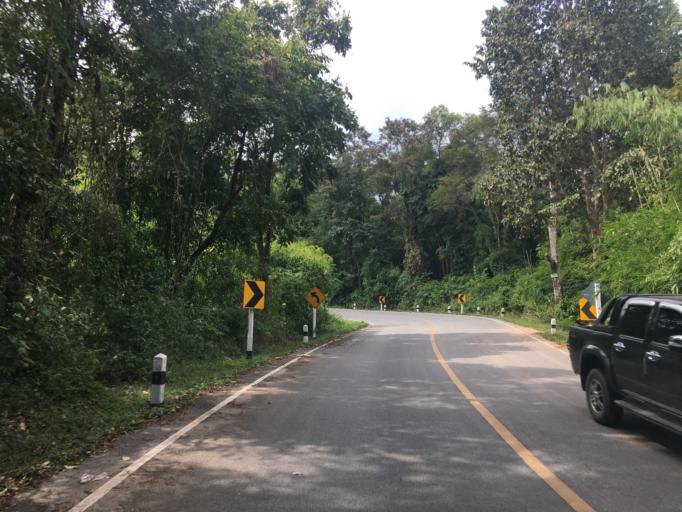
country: TH
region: Nan
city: Ban Luang
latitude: 18.8774
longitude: 100.5423
